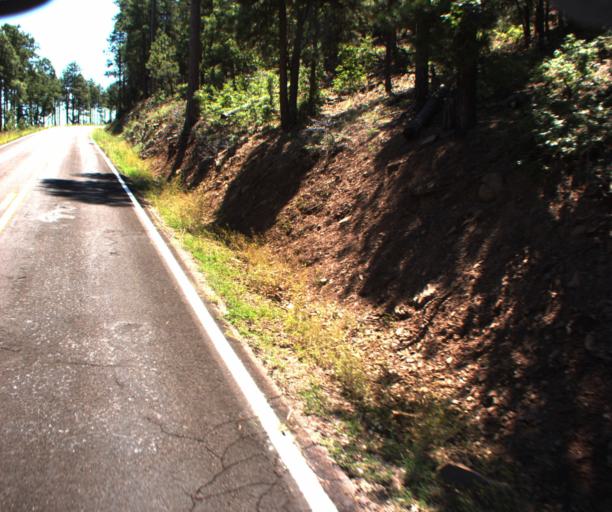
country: US
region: Arizona
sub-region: Greenlee County
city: Morenci
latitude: 33.4665
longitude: -109.3610
